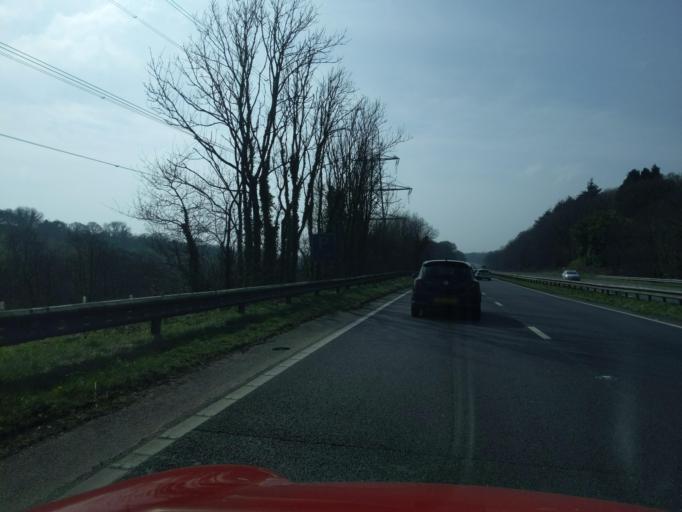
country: GB
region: England
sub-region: Devon
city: Ivybridge
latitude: 50.3947
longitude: -3.8727
